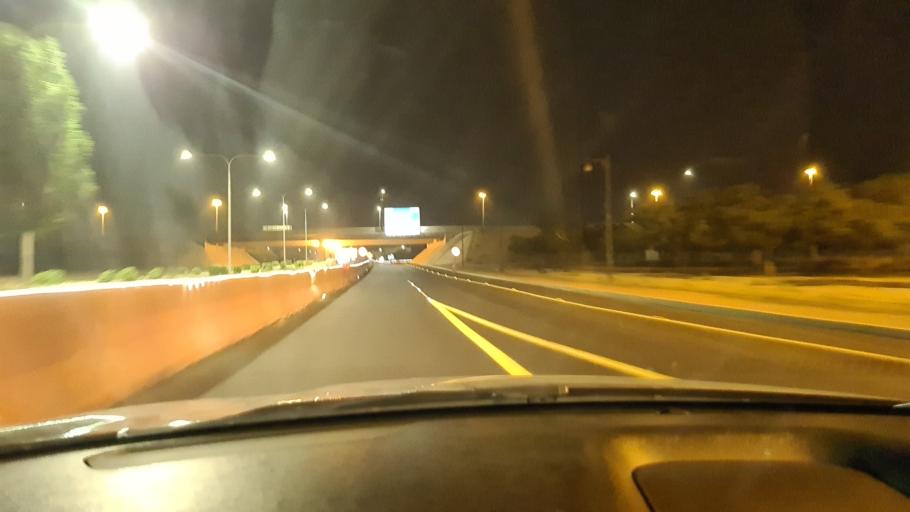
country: SA
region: Eastern Province
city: Al Jubayl
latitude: 27.1358
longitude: 49.5564
